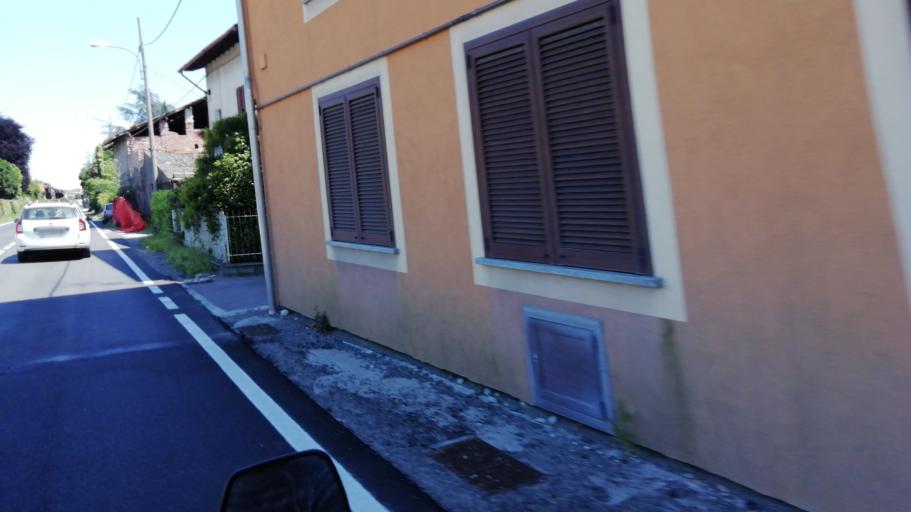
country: IT
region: Piedmont
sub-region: Provincia di Novara
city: Oleggio
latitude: 45.5925
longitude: 8.6505
